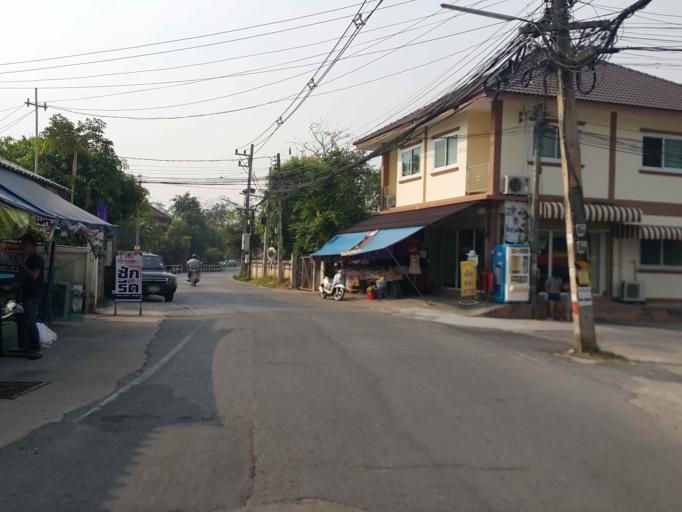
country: TH
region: Chiang Mai
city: Saraphi
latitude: 18.7749
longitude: 99.0533
